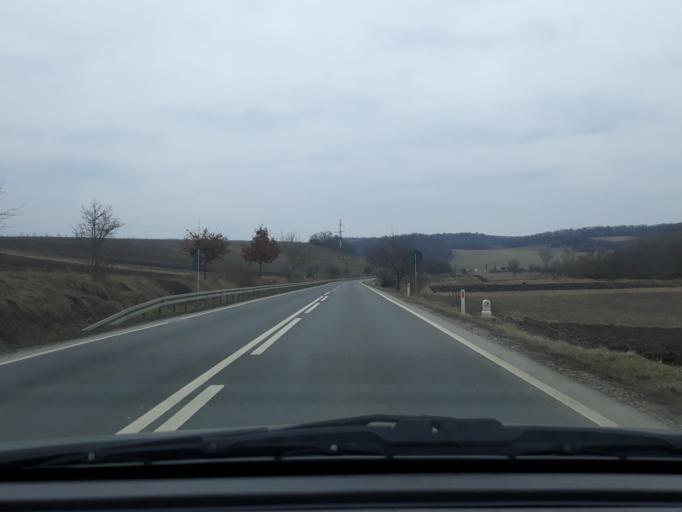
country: RO
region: Salaj
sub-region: Comuna Nusfalau
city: Nusfalau
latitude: 47.2208
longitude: 22.7369
